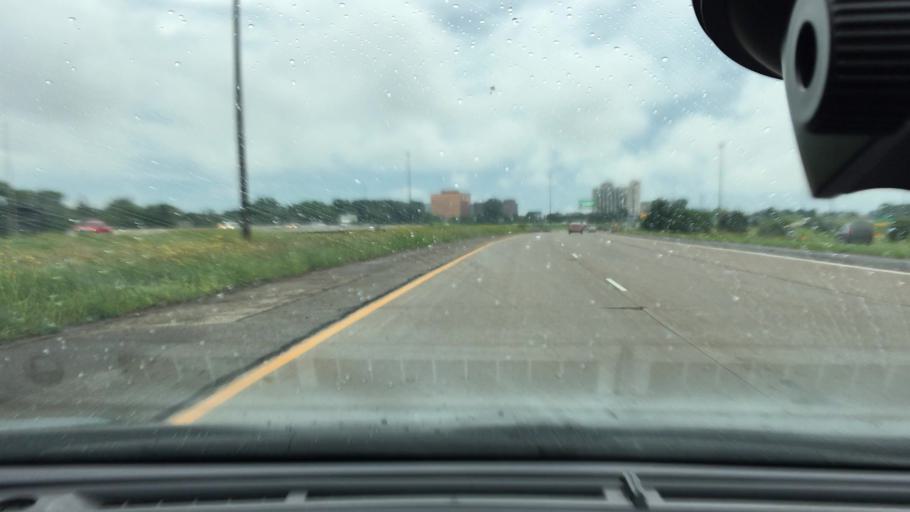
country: US
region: Minnesota
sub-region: Dakota County
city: Mendota Heights
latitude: 44.8641
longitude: -93.2075
